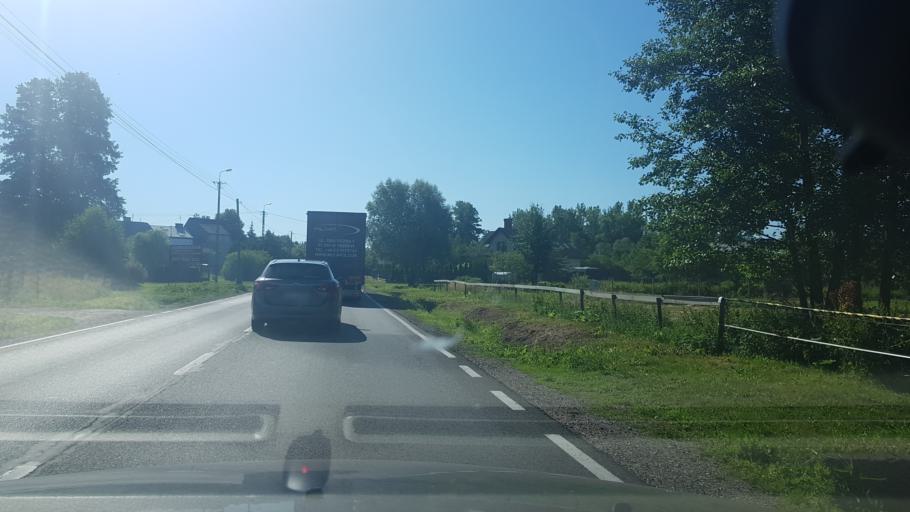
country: PL
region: Masovian Voivodeship
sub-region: Powiat wegrowski
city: Lochow
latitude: 52.5446
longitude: 21.6401
